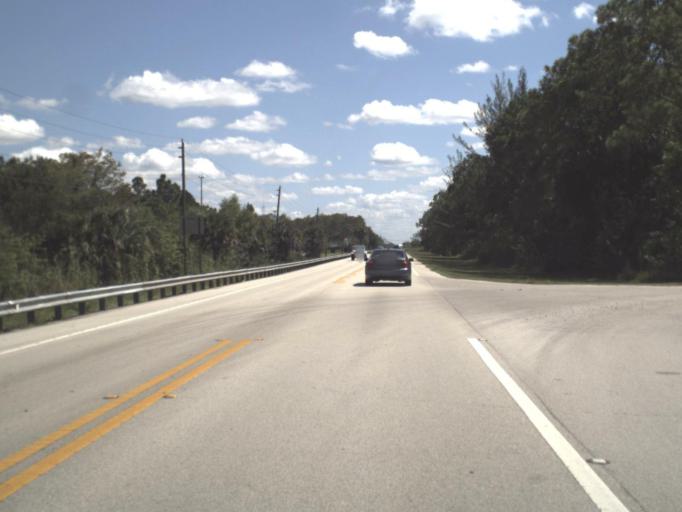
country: US
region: Florida
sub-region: Collier County
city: Lely Resort
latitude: 26.0234
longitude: -81.6367
